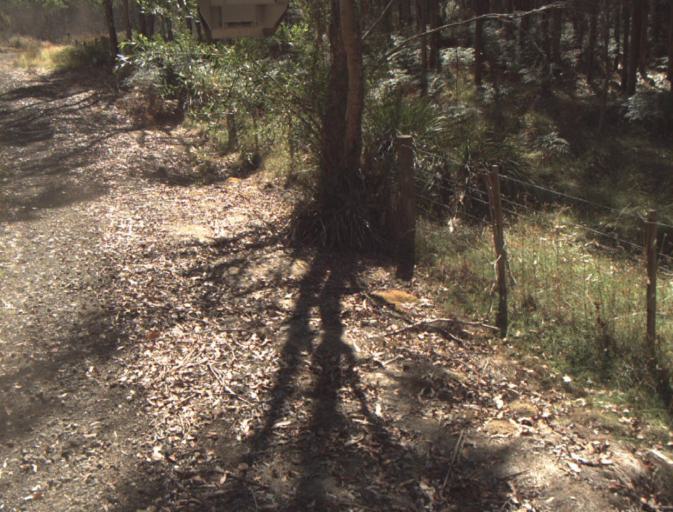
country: AU
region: Tasmania
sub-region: Launceston
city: Newstead
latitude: -41.3056
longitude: 147.3119
